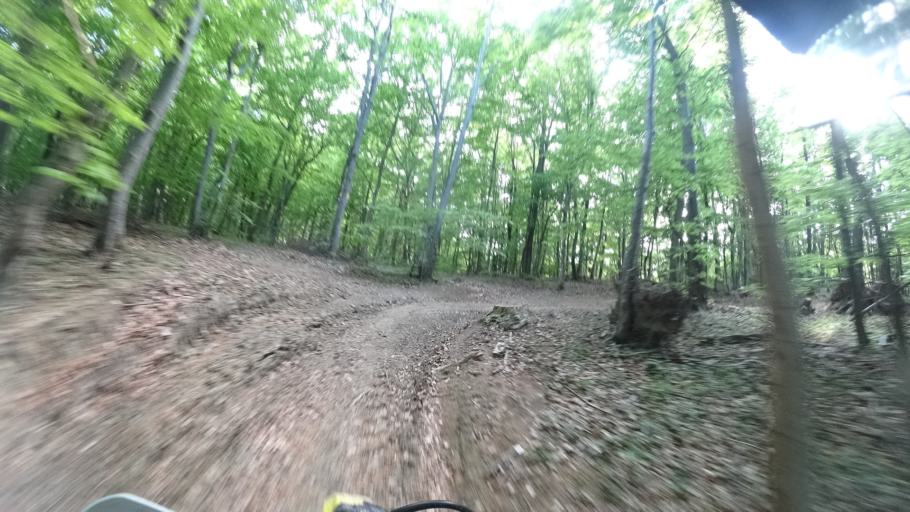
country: HR
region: Zagrebacka
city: Jablanovec
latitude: 45.8661
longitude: 15.8794
